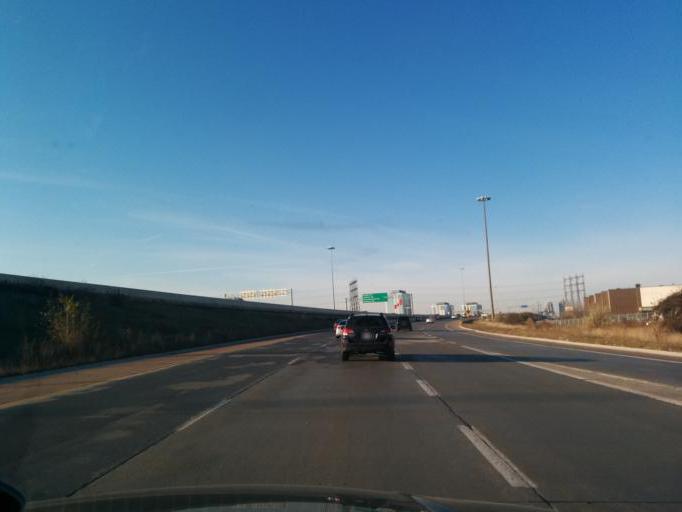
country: CA
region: Ontario
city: Etobicoke
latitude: 43.6166
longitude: -79.5519
